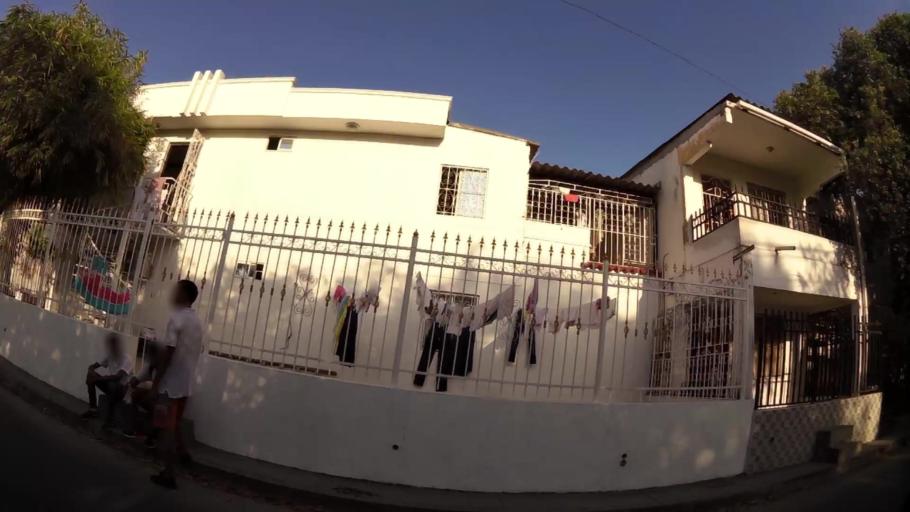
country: CO
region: Bolivar
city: Cartagena
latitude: 10.3878
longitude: -75.4814
